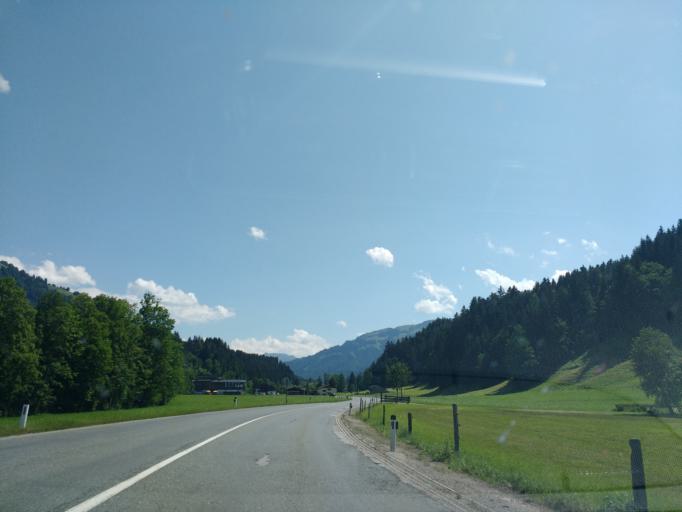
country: AT
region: Tyrol
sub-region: Politischer Bezirk Kitzbuhel
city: Oberndorf in Tirol
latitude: 47.4804
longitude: 12.3822
